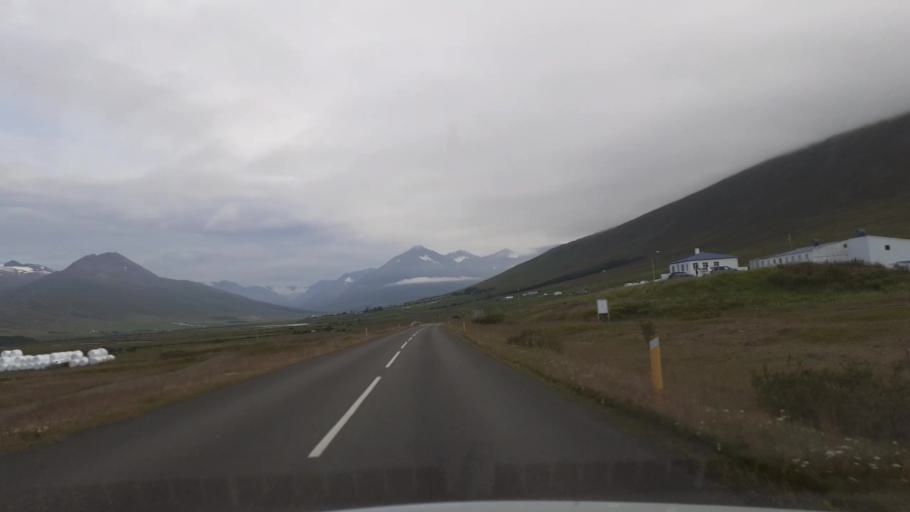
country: IS
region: Northeast
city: Dalvik
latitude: 65.9480
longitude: -18.5563
